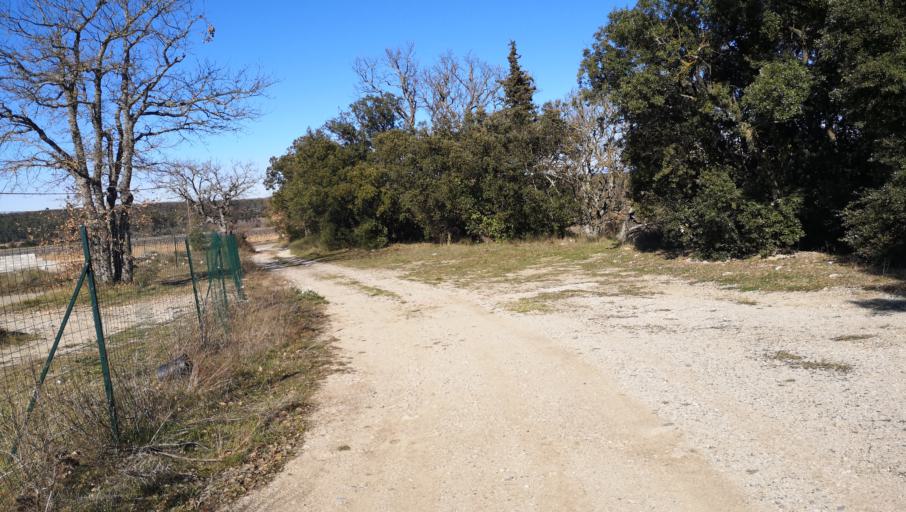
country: FR
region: Provence-Alpes-Cote d'Azur
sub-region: Departement du Var
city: Ginasservis
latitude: 43.5936
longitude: 5.8633
